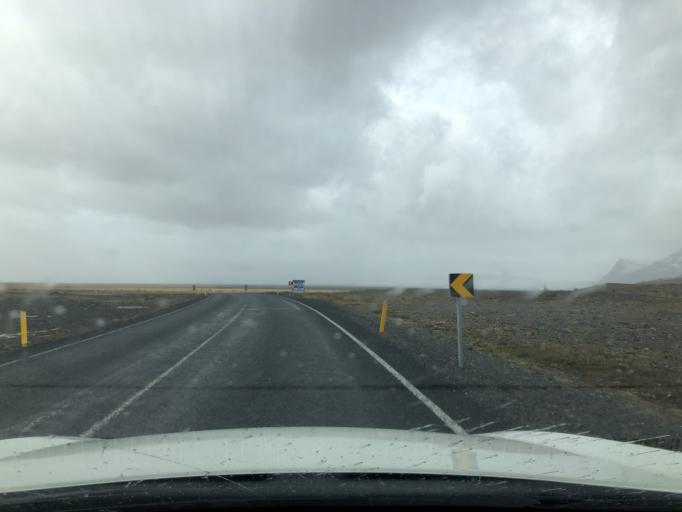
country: IS
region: East
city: Hoefn
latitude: 64.0066
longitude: -16.9371
